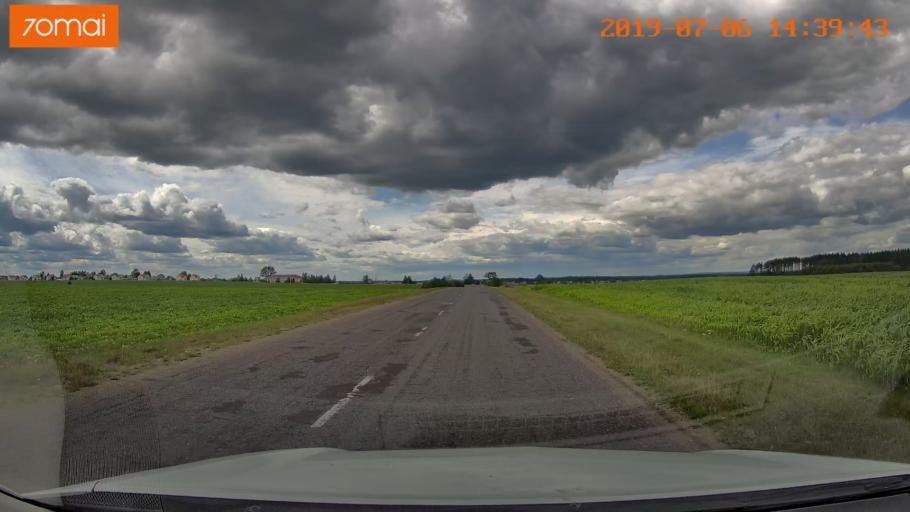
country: BY
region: Minsk
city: Ivyanyets
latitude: 53.9189
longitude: 26.6844
